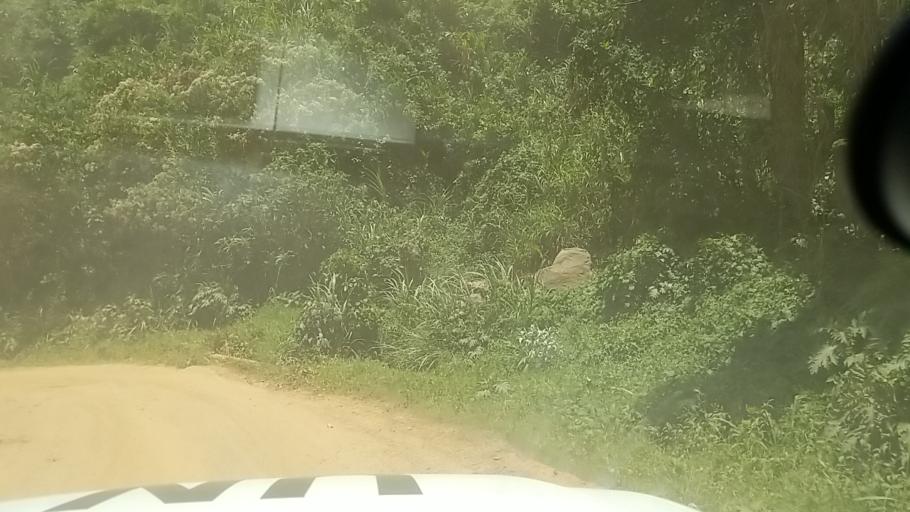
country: CD
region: Nord Kivu
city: Sake
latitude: -1.8324
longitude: 29.0012
